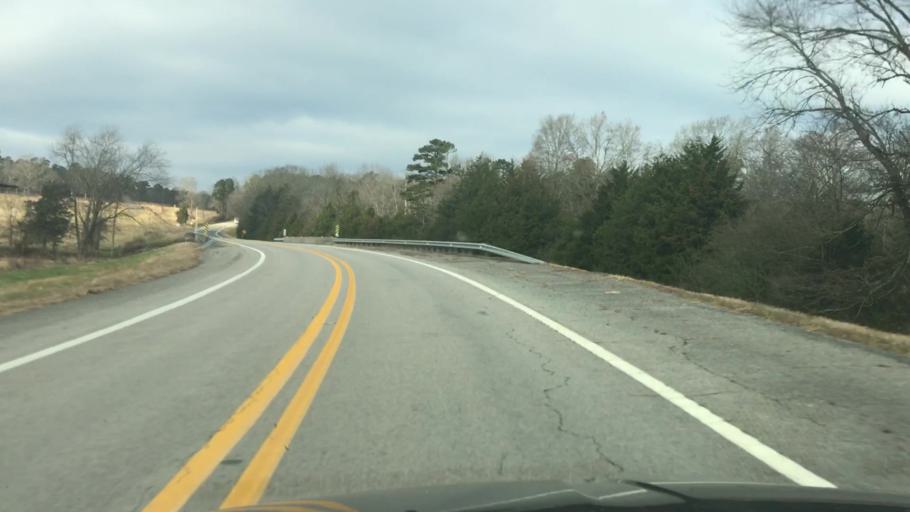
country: US
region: Arkansas
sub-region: Montgomery County
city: Mount Ida
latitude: 34.6590
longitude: -93.7626
